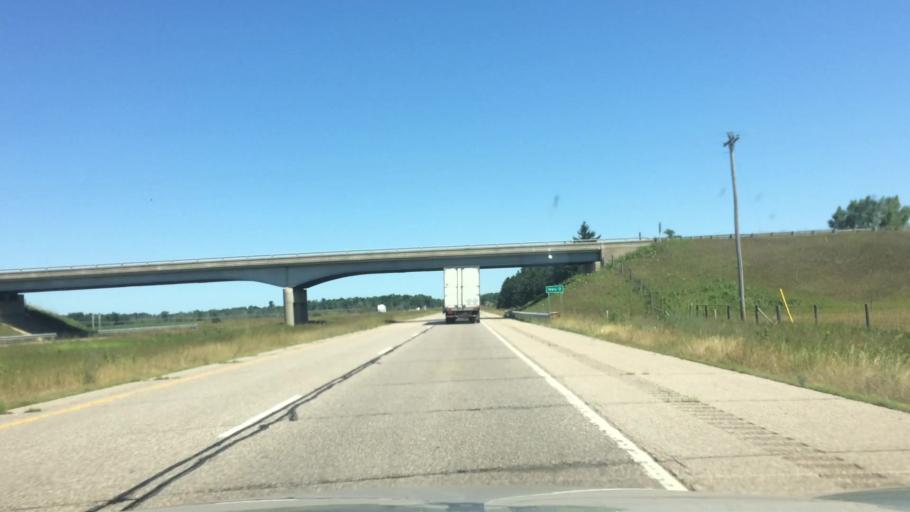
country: US
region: Wisconsin
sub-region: Waushara County
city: Wautoma
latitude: 44.1550
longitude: -89.5323
